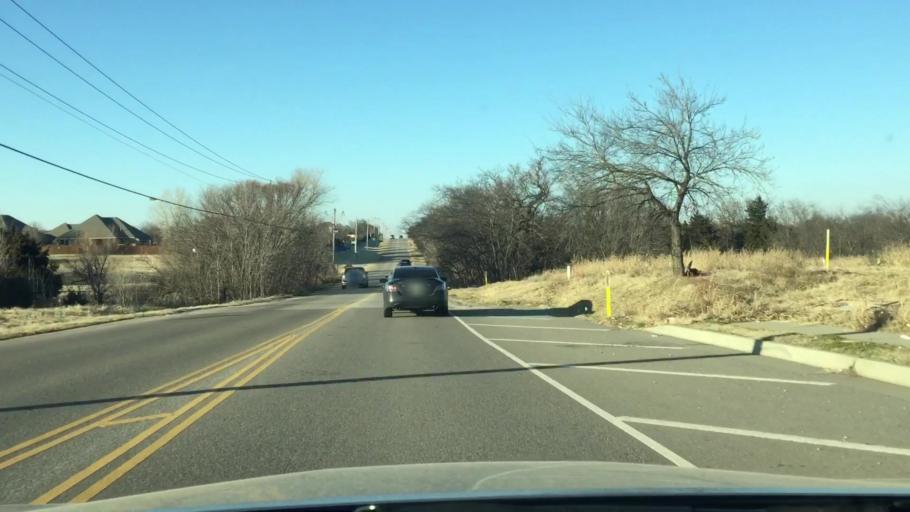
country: US
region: Oklahoma
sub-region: Oklahoma County
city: The Village
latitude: 35.6248
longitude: -97.6208
